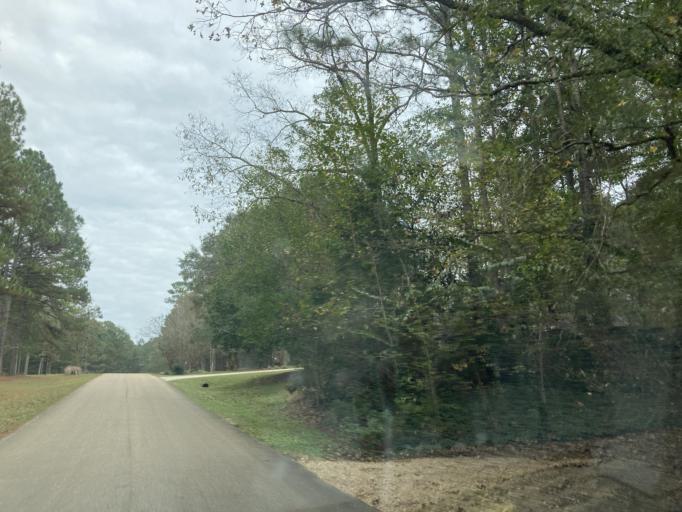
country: US
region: Mississippi
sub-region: Lamar County
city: West Hattiesburg
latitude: 31.3021
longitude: -89.4487
